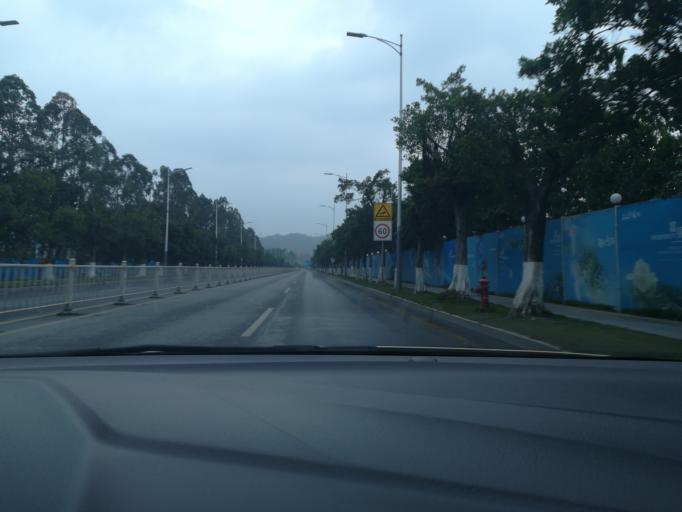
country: CN
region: Guangdong
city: Nansha
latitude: 22.7756
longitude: 113.5952
